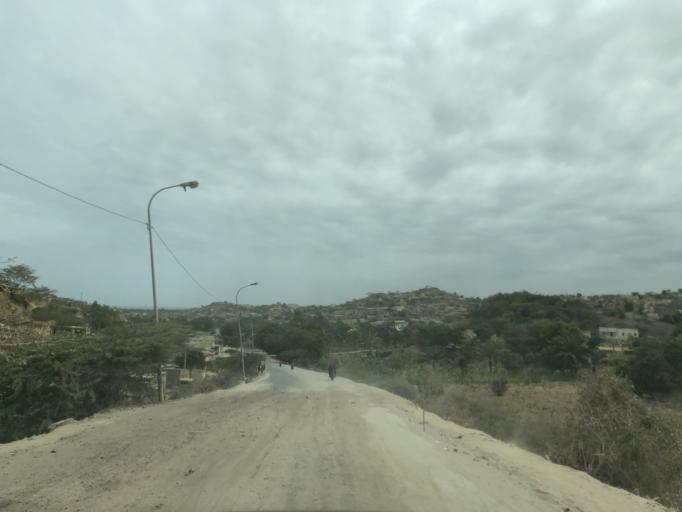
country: AO
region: Cuanza Sul
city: Sumbe
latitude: -11.2211
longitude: 13.8476
